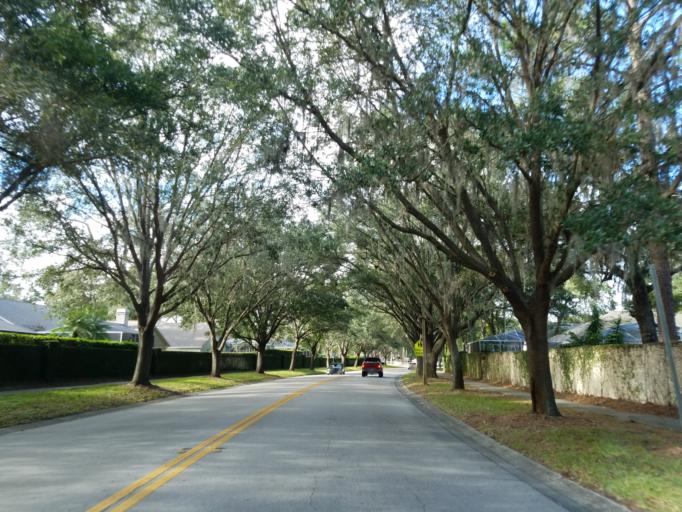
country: US
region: Florida
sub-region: Hillsborough County
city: Bloomingdale
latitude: 27.8852
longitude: -82.2467
